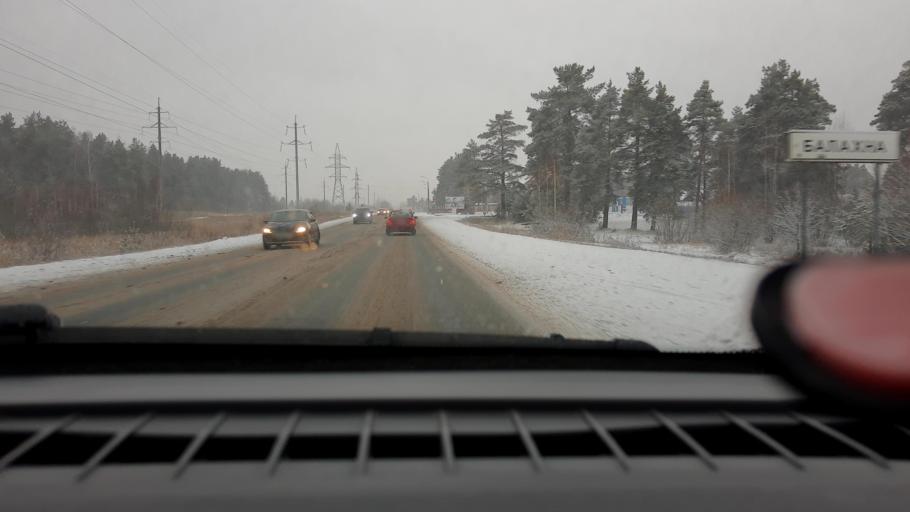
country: RU
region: Nizjnij Novgorod
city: Novaya Balakhna
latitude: 56.4698
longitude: 43.6143
